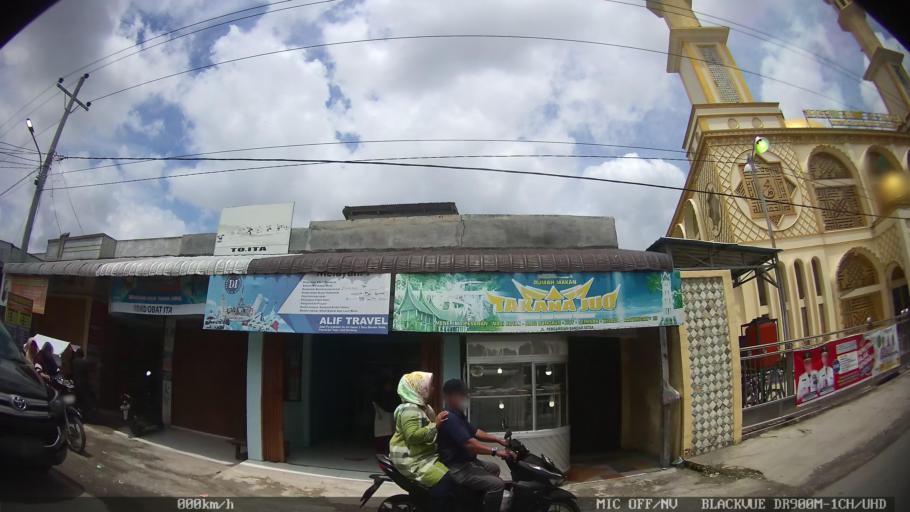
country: ID
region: North Sumatra
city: Medan
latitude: 3.6208
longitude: 98.7483
